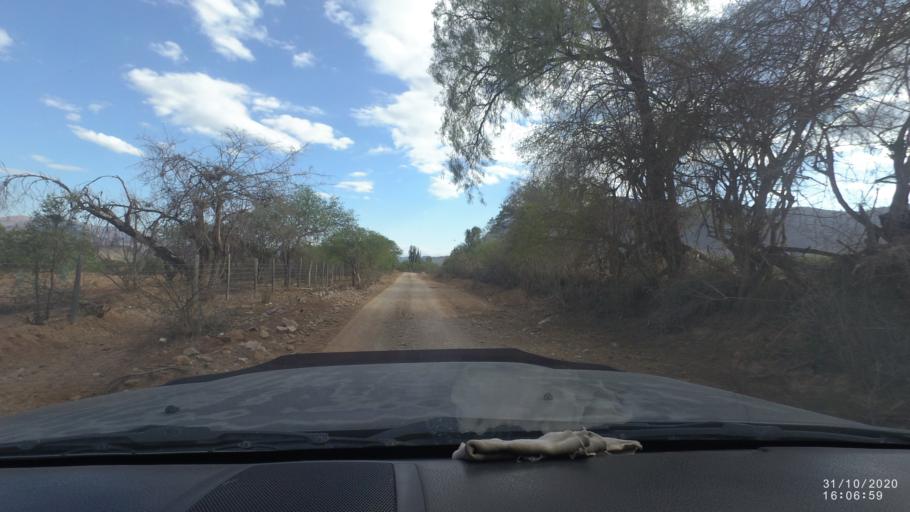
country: BO
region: Chuquisaca
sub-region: Provincia Zudanez
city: Mojocoya
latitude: -18.3770
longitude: -64.6458
